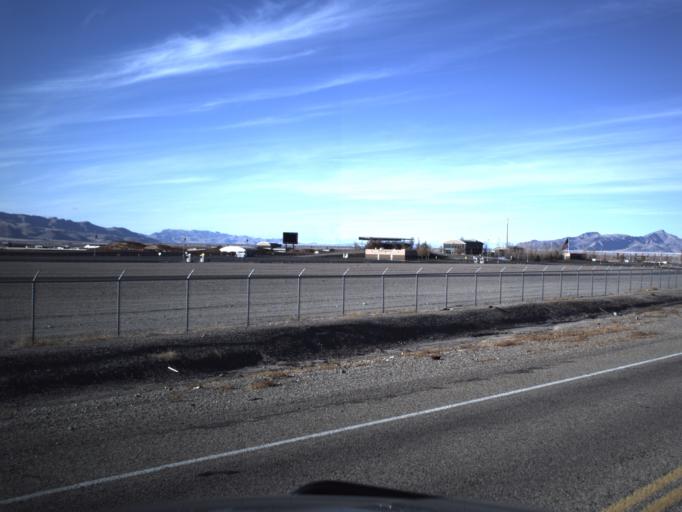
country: US
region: Utah
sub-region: Tooele County
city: Erda
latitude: 40.5766
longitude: -112.3674
